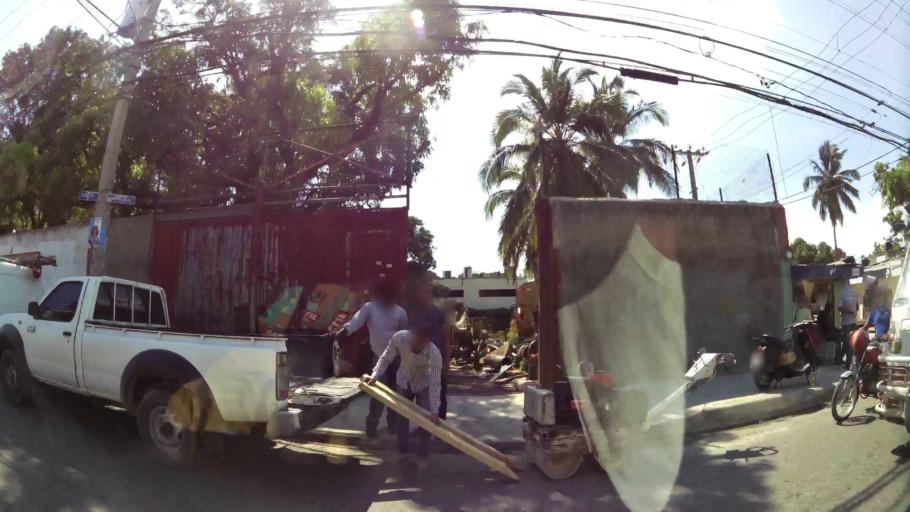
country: DO
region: Nacional
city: Santo Domingo
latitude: 18.4823
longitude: -69.9804
